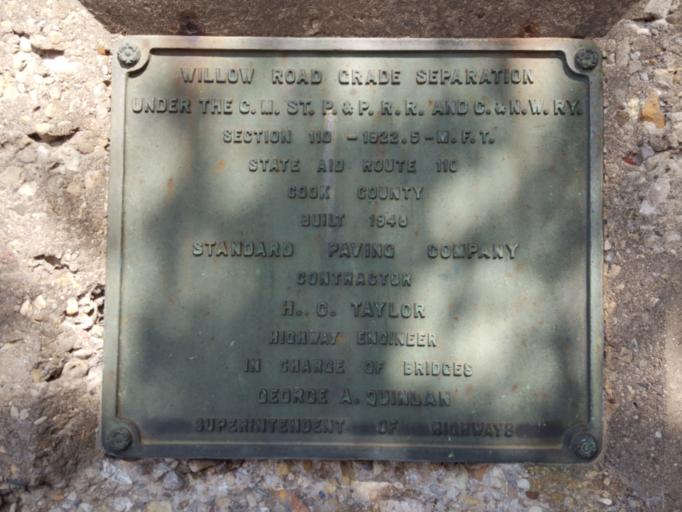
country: US
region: Illinois
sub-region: Cook County
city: Northbrook
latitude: 42.1055
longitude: -87.8276
